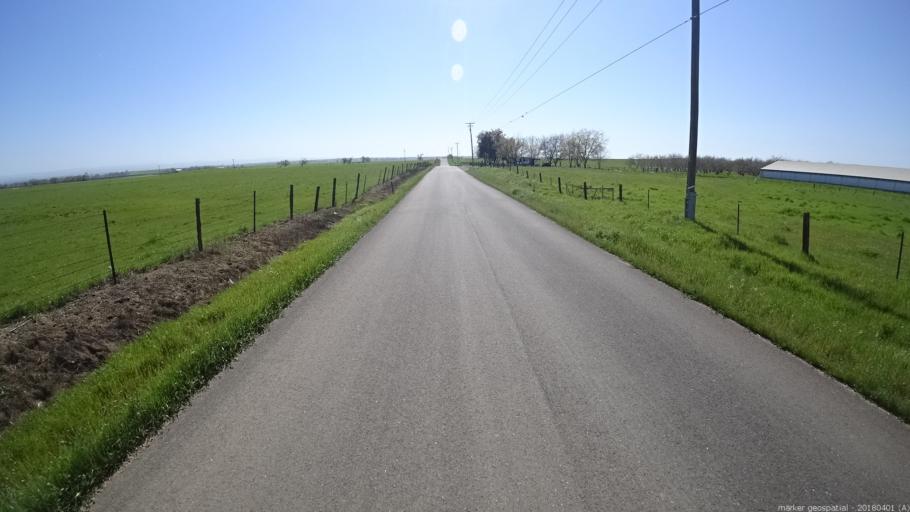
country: US
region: California
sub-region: Sacramento County
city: Rancho Murieta
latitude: 38.4735
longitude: -121.1695
